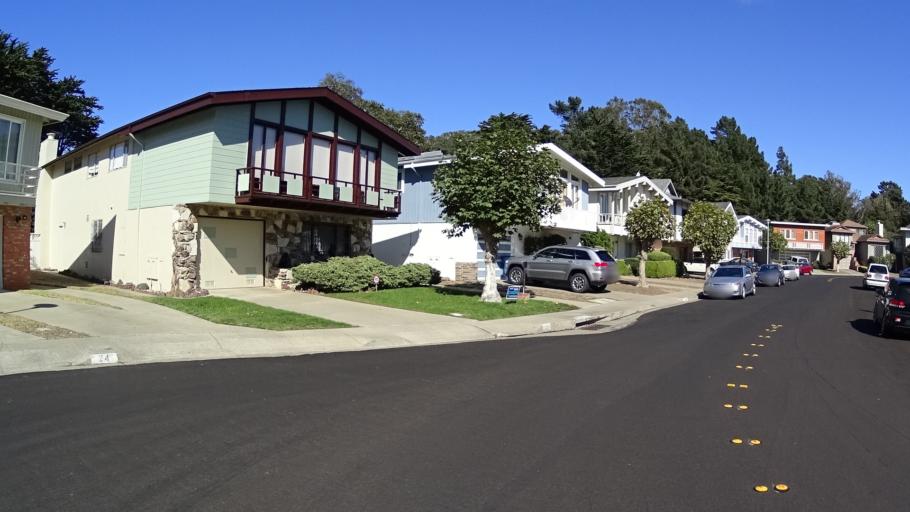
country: US
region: California
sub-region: San Mateo County
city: Broadmoor
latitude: 37.7079
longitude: -122.4851
